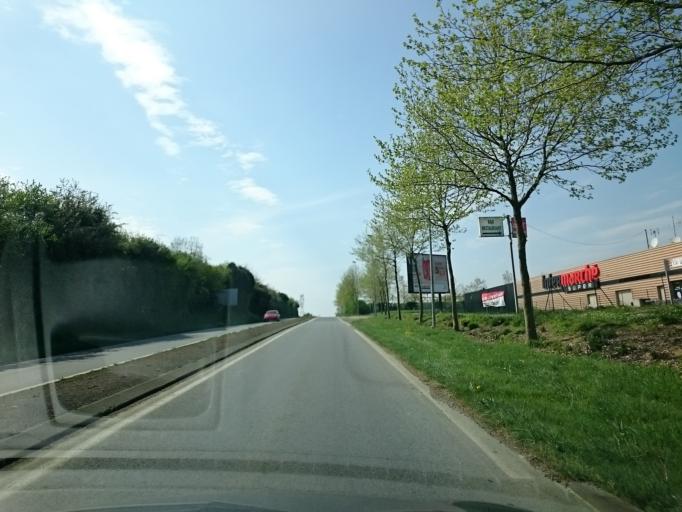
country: FR
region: Brittany
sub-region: Departement d'Ille-et-Vilaine
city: Chateaugiron
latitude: 48.0556
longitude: -1.5258
